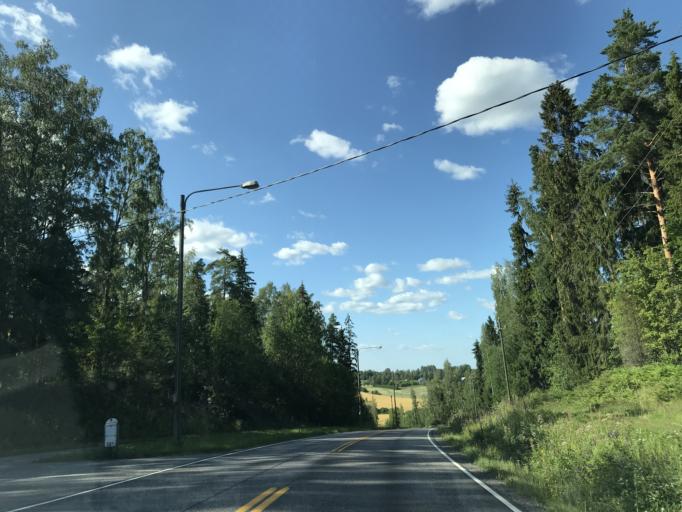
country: FI
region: Uusimaa
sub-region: Helsinki
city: Nurmijaervi
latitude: 60.4148
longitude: 24.8757
